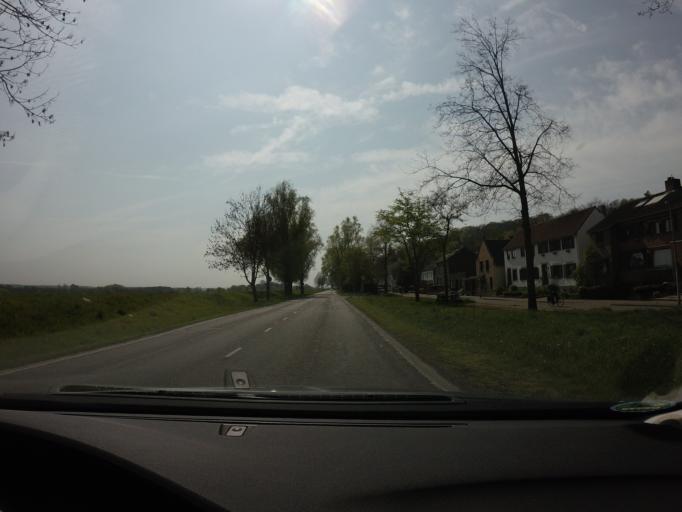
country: NL
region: Limburg
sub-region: Gemeente Maastricht
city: Maastricht
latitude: 50.8297
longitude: 5.6959
